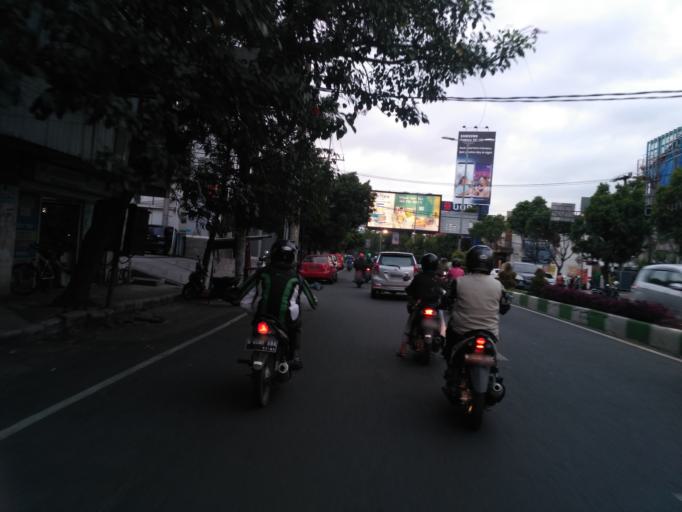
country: ID
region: East Java
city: Malang
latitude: -7.9766
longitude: 112.6294
